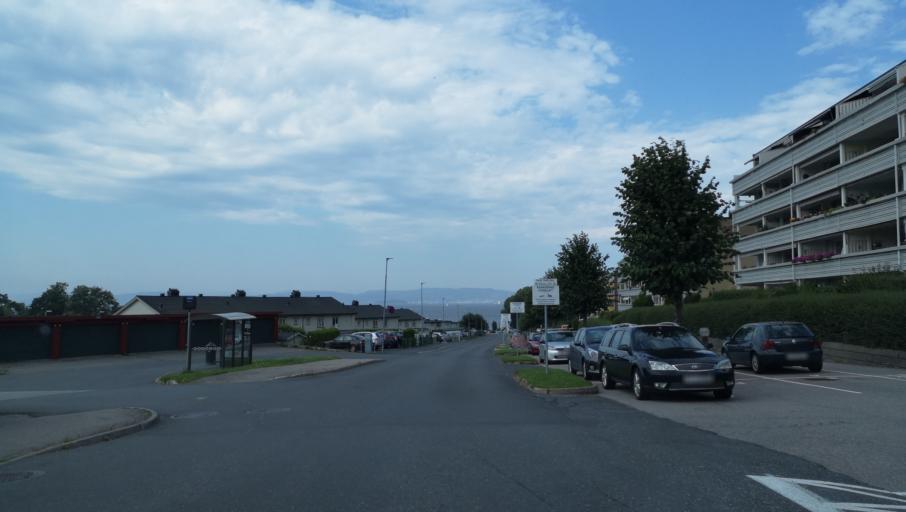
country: NO
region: Ostfold
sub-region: Moss
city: Moss
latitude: 59.4445
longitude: 10.6182
